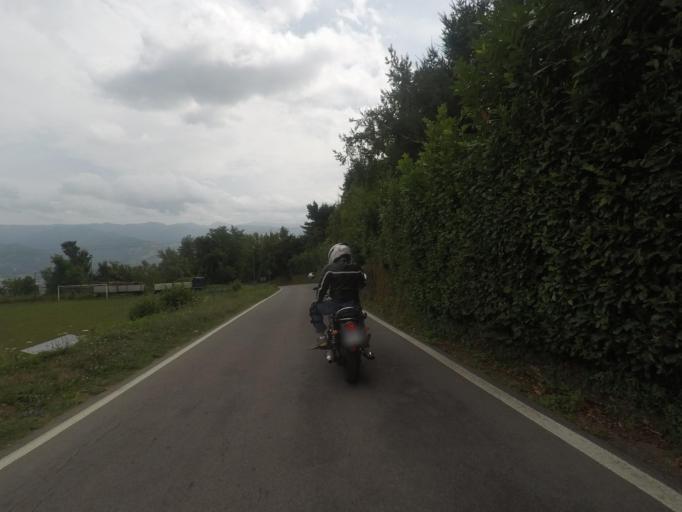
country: IT
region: Tuscany
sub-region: Provincia di Lucca
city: Castelnuovo di Garfagnana
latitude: 44.1120
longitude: 10.3772
